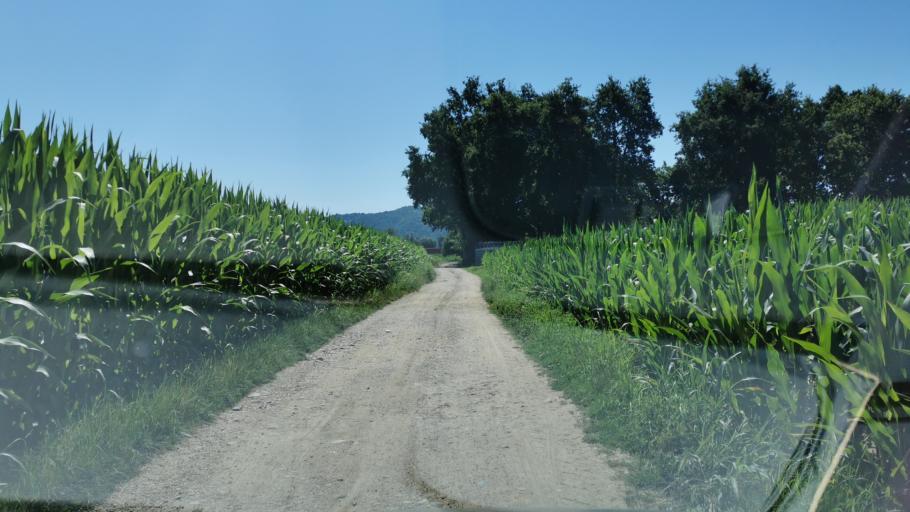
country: IT
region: Piedmont
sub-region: Provincia di Torino
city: Brandizzo
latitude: 45.1894
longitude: 7.8363
